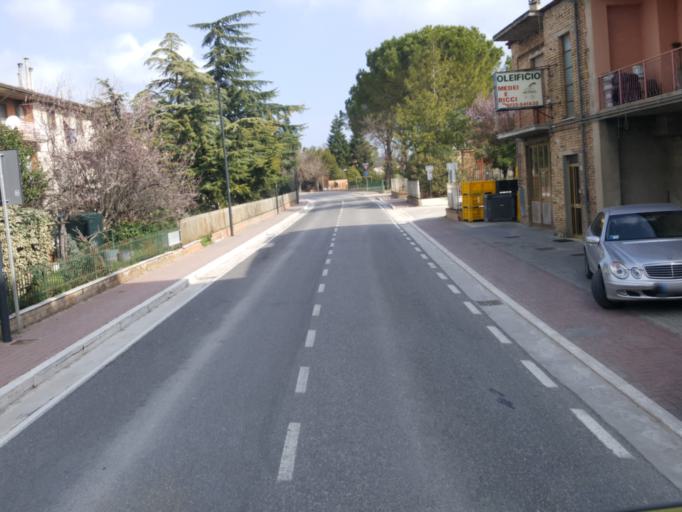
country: IT
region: The Marches
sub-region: Provincia di Macerata
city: Passo di Treia
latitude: 43.2844
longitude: 13.3330
